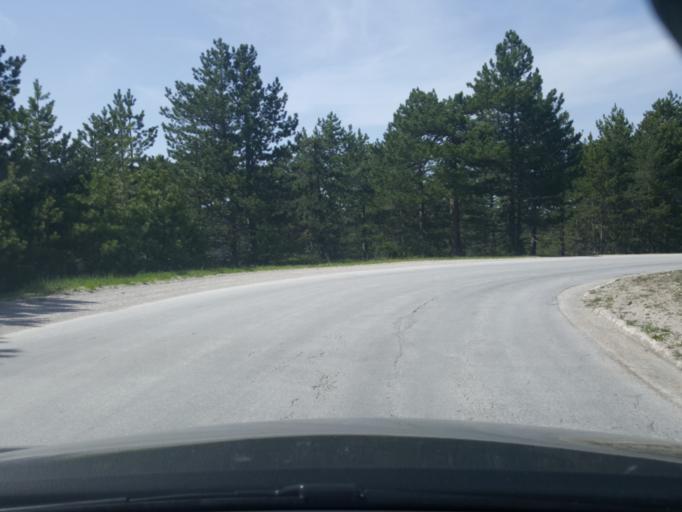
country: RS
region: Central Serbia
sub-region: Zlatiborski Okrug
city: Bajina Basta
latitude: 43.8840
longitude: 19.5418
